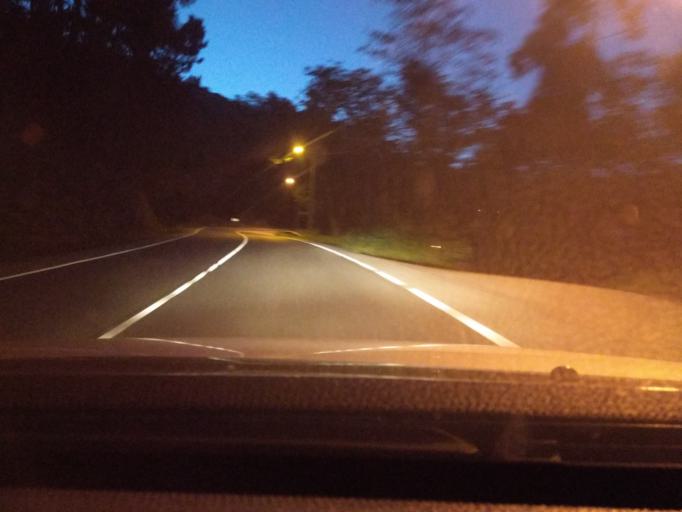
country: ES
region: Galicia
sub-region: Provincia de Pontevedra
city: Moana
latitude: 42.2994
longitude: -8.7428
